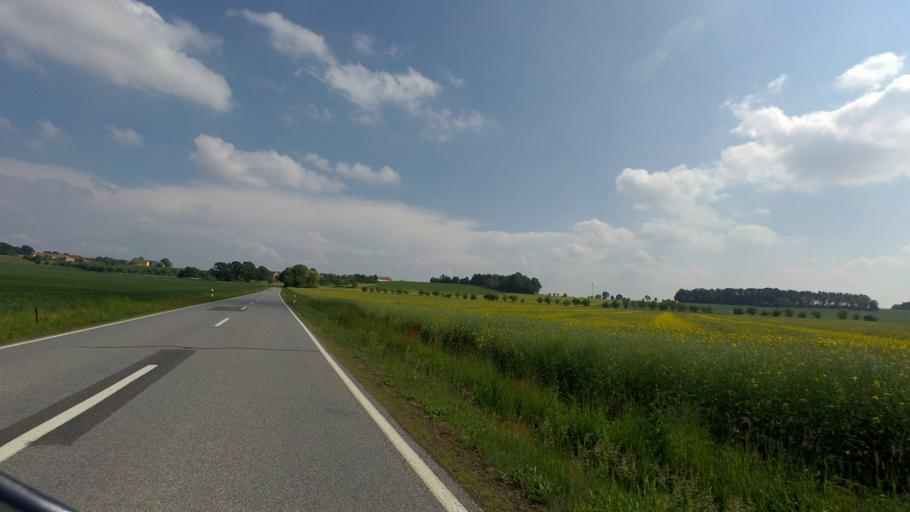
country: DE
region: Saxony
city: Guttau
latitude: 51.2174
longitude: 14.5989
